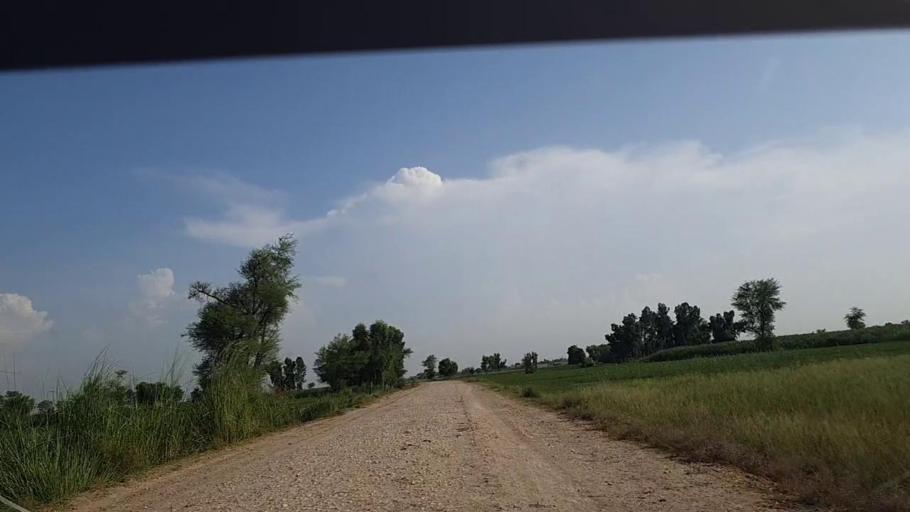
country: PK
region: Sindh
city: Khanpur
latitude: 27.8655
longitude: 69.3748
